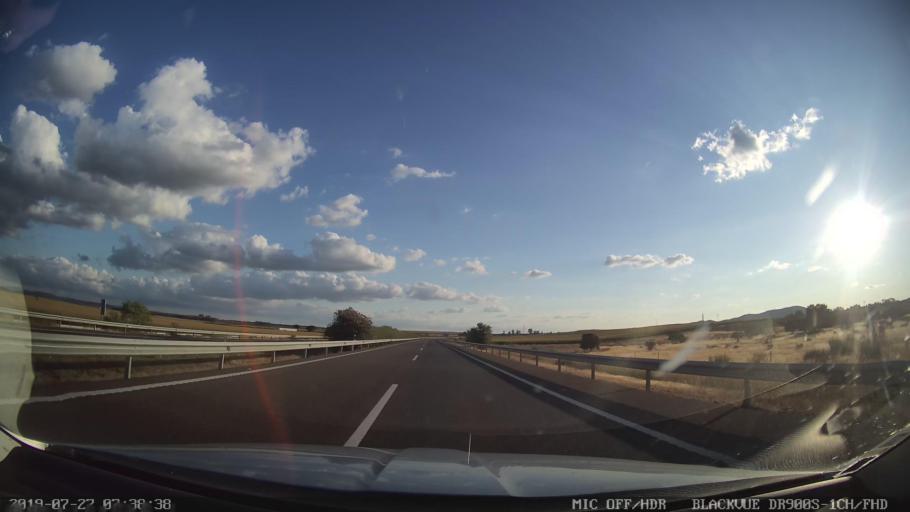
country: ES
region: Extremadura
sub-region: Provincia de Badajoz
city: Santa Amalia
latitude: 39.0724
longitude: -6.0386
